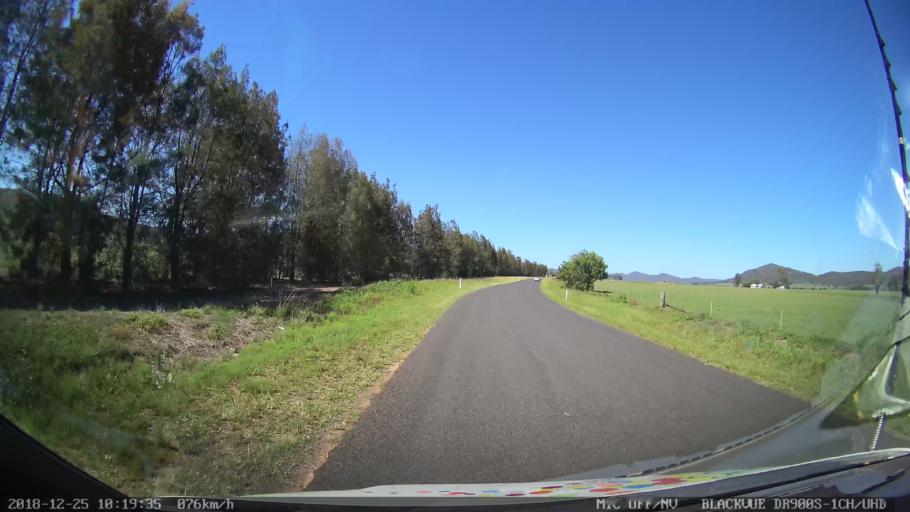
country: AU
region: New South Wales
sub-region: Muswellbrook
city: Denman
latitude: -32.3521
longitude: 150.5574
